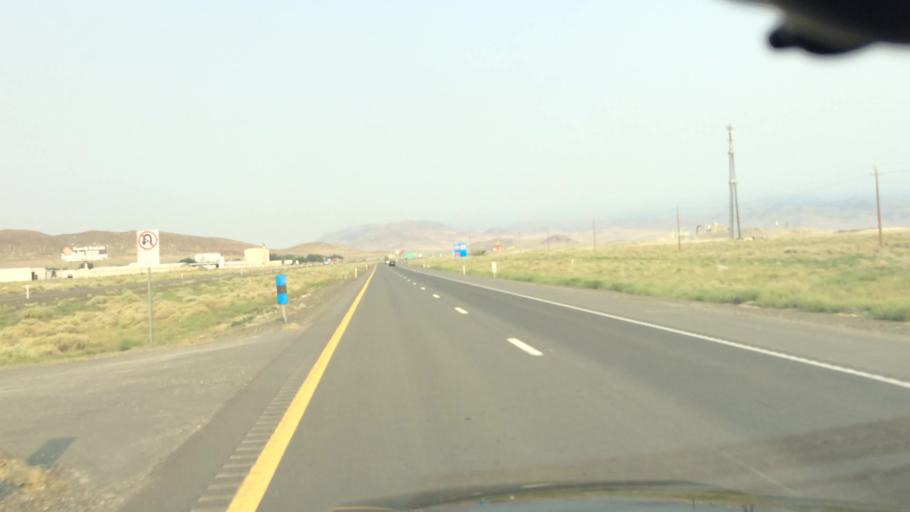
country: US
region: Nevada
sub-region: Lyon County
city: Fernley
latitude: 39.6154
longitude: -119.2492
